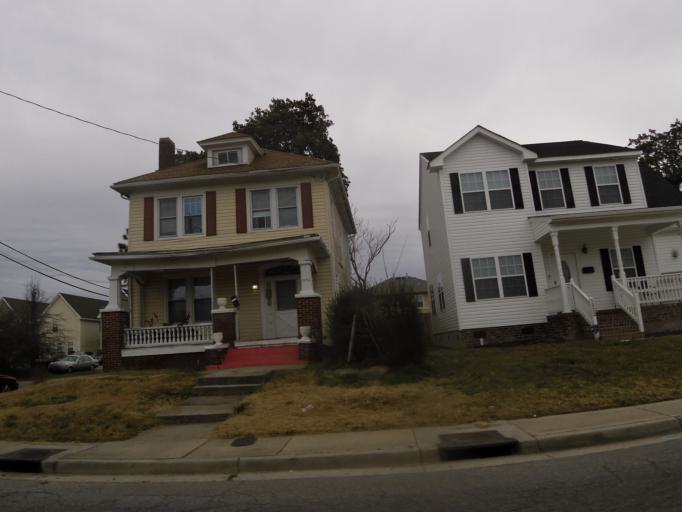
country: US
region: Virginia
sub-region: City of Portsmouth
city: Portsmouth
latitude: 36.8334
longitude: -76.3182
